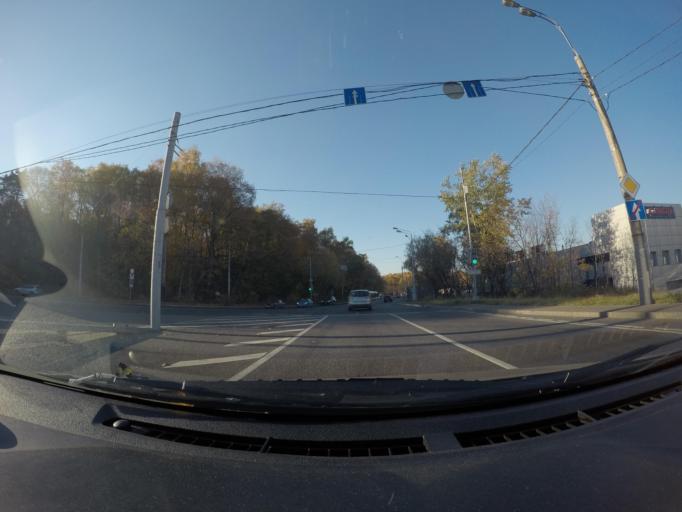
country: RU
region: Moscow
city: Sokol'niki
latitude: 55.8138
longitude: 37.6875
